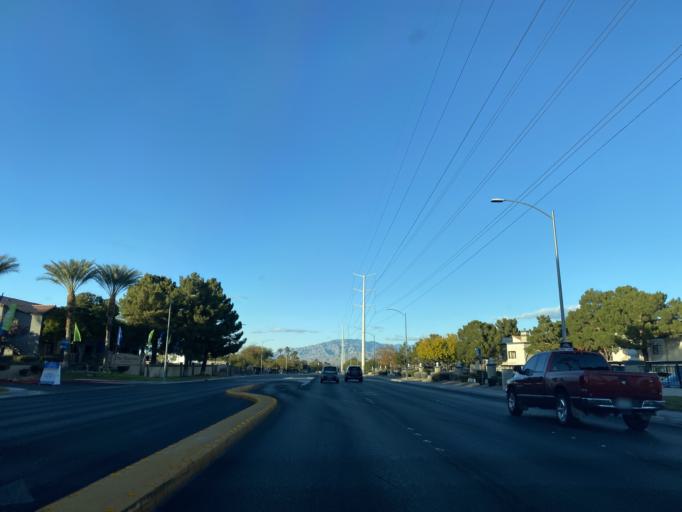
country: US
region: Nevada
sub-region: Clark County
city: Spring Valley
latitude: 36.1997
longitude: -115.2605
